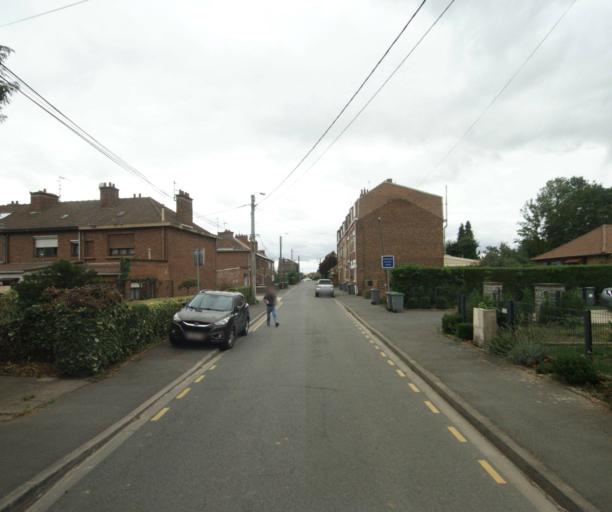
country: FR
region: Nord-Pas-de-Calais
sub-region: Departement du Nord
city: Fretin
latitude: 50.5612
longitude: 3.1361
